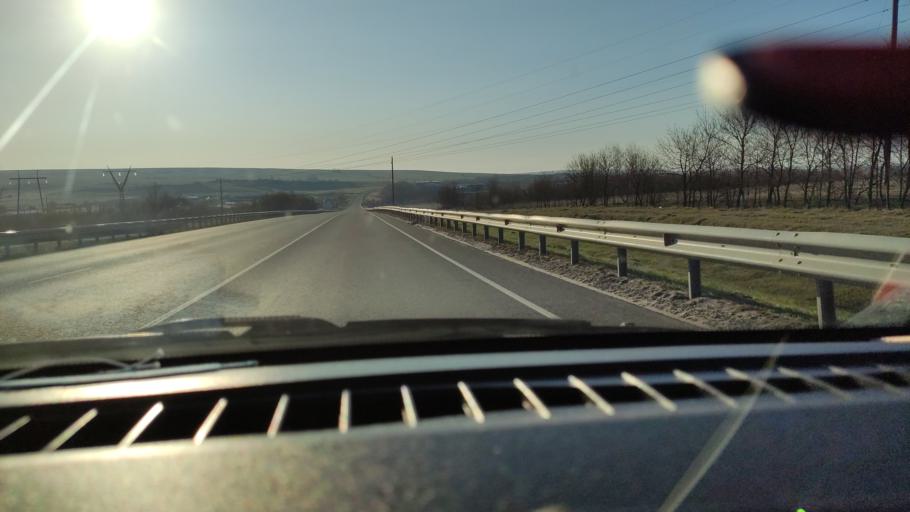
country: RU
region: Saratov
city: Tersa
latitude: 52.0996
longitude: 47.5196
